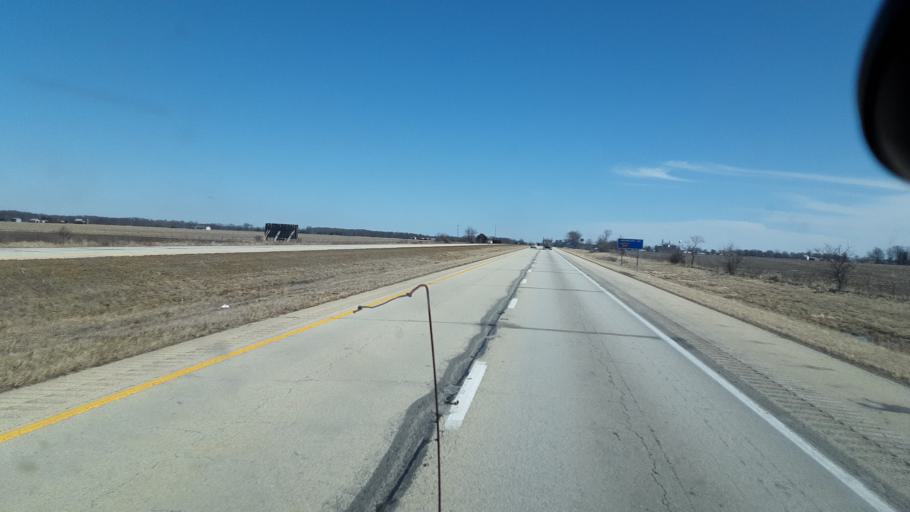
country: US
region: Illinois
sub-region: Effingham County
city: Teutopolis
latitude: 39.1643
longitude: -88.4091
